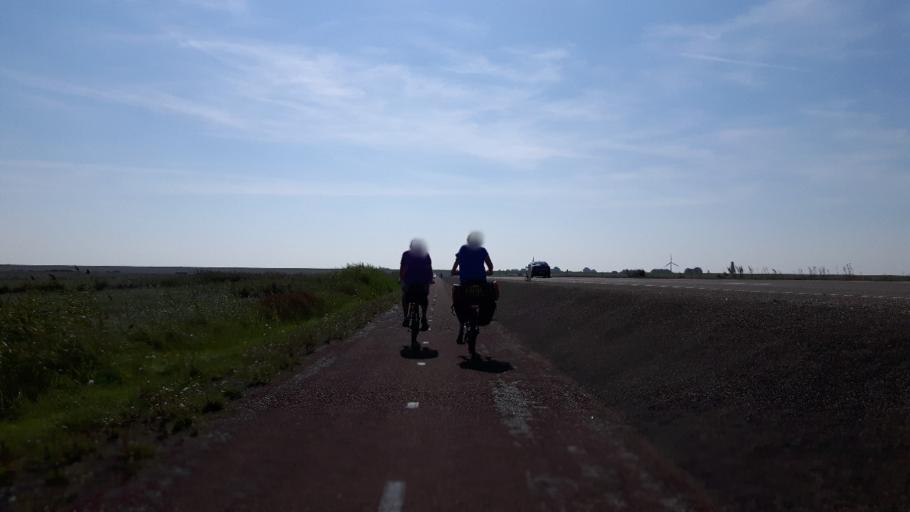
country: NL
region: Friesland
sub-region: Gemeente Dongeradeel
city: Holwerd
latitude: 53.3862
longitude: 5.8880
